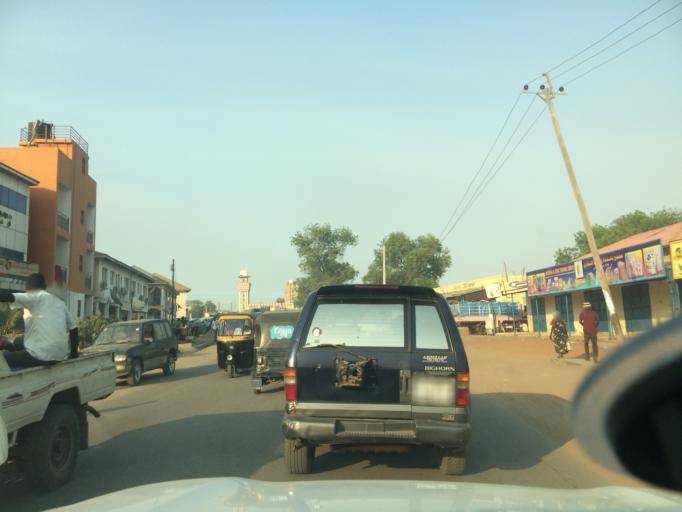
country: SS
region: Central Equatoria
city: Juba
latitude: 4.8310
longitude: 31.6096
